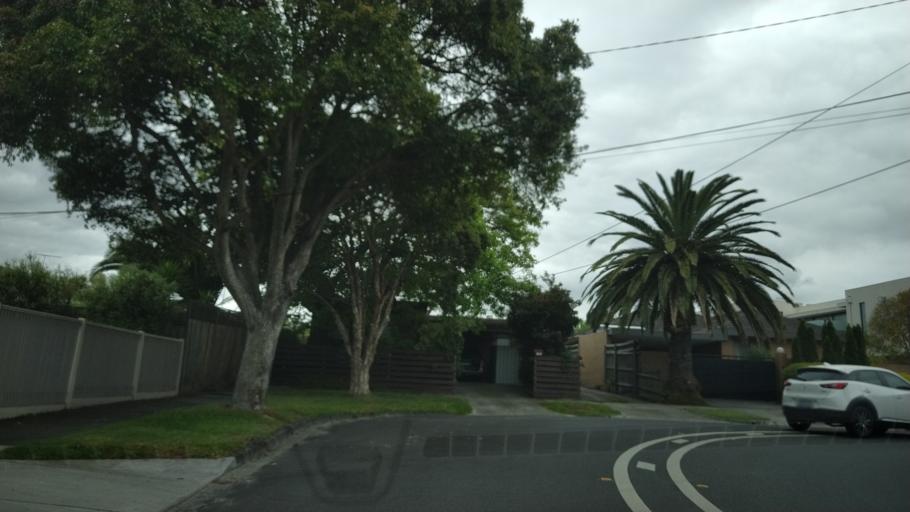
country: AU
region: Victoria
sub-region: Glen Eira
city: Caulfield
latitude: -37.8841
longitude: 145.0261
